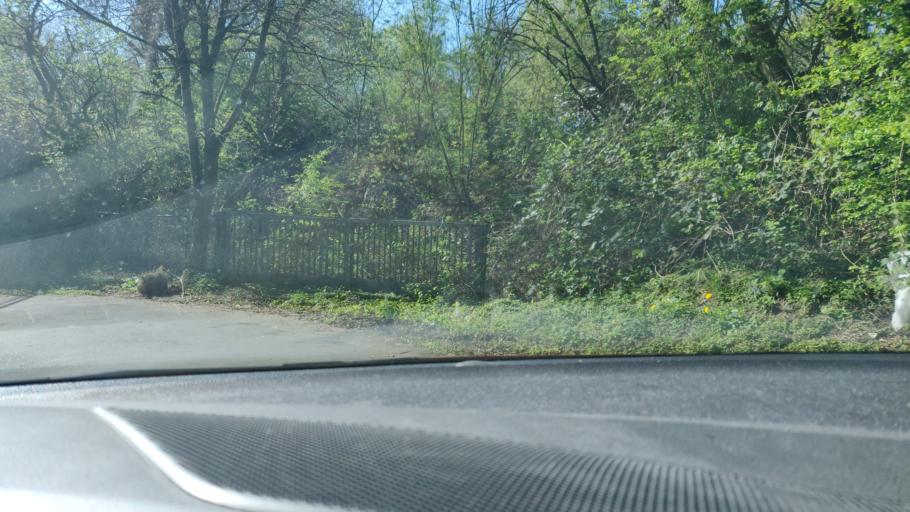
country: DE
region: North Rhine-Westphalia
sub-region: Regierungsbezirk Dusseldorf
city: Velbert
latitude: 51.3349
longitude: 7.0589
